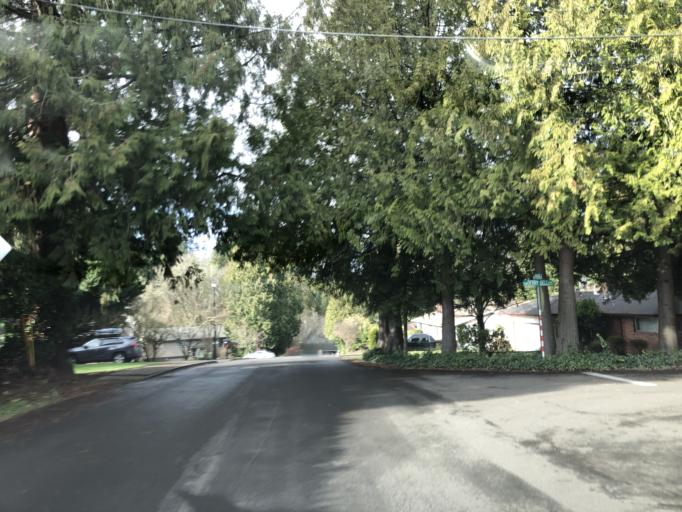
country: US
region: Oregon
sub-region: Washington County
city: Tigard
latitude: 45.4241
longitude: -122.7890
